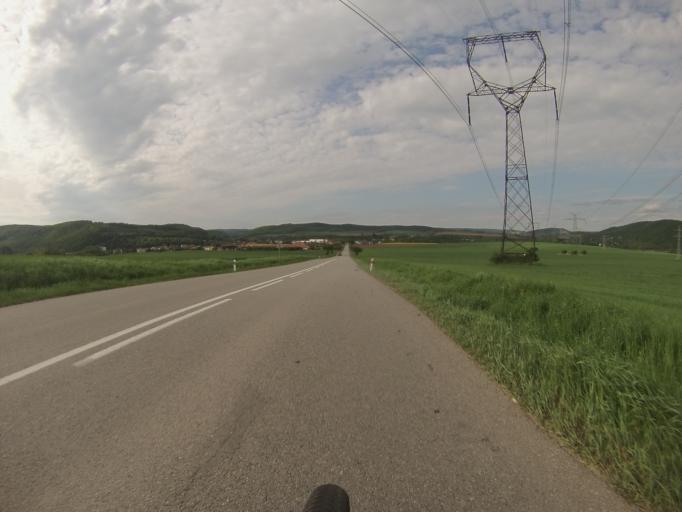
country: CZ
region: South Moravian
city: Veverska Bityska
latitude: 49.2652
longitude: 16.4408
